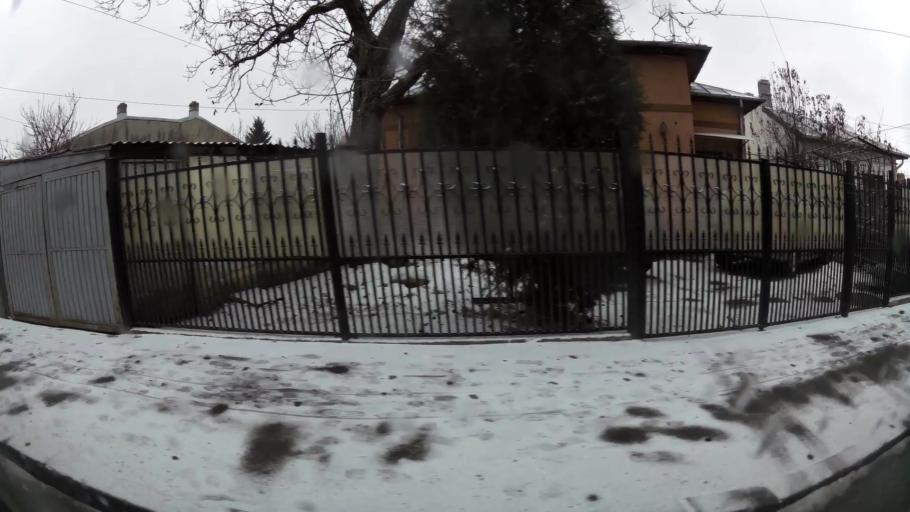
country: RO
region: Prahova
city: Ploiesti
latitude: 44.9491
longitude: 26.0268
